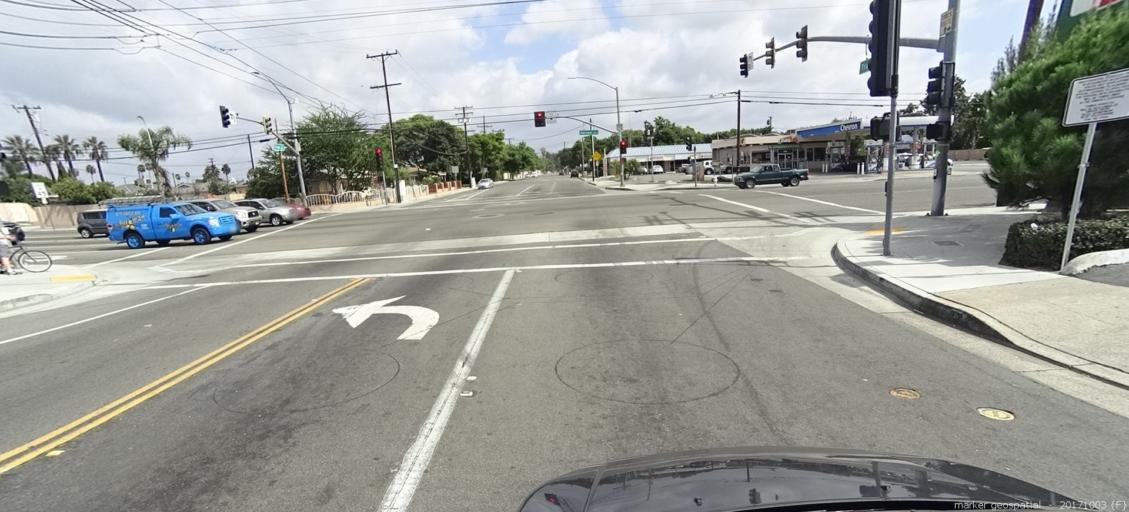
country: US
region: California
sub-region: Orange County
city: Garden Grove
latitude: 33.7671
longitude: -117.9033
